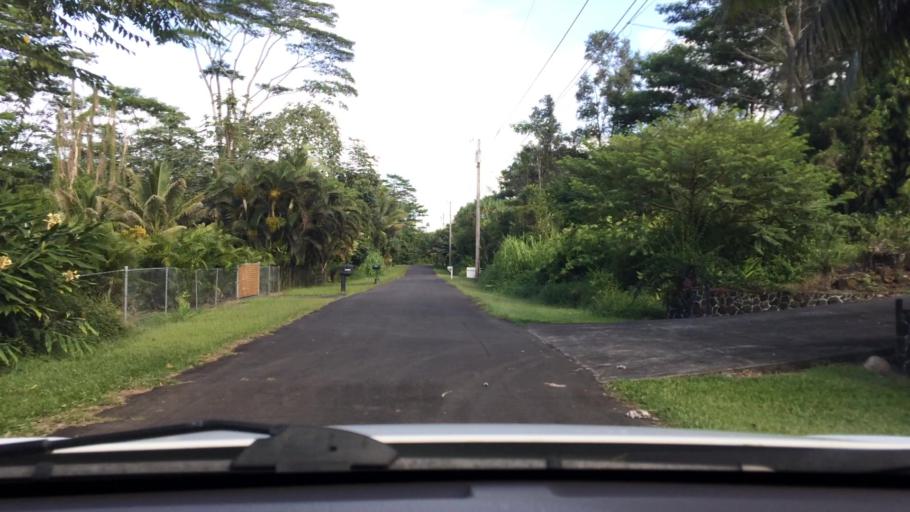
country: US
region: Hawaii
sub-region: Hawaii County
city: Hawaiian Beaches
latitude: 19.5445
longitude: -154.8989
